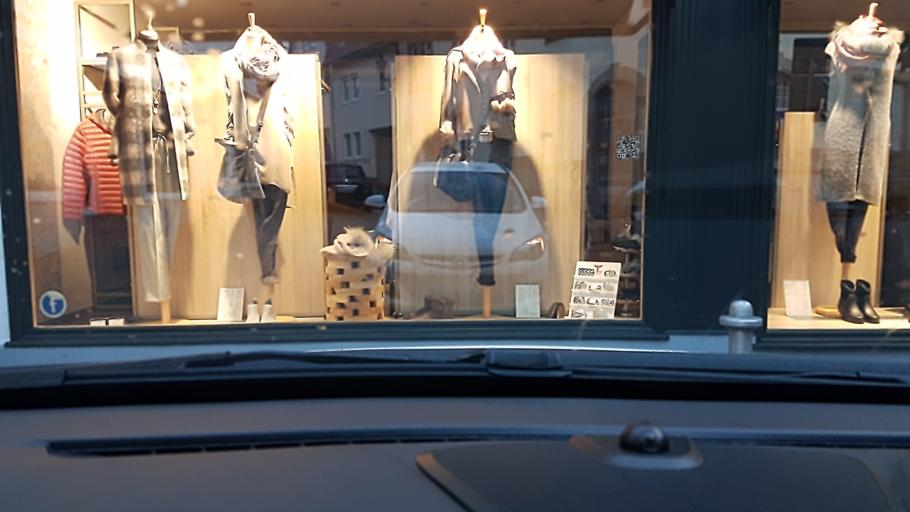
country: DE
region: Hesse
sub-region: Regierungsbezirk Darmstadt
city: Oberursel
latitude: 50.2022
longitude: 8.5776
